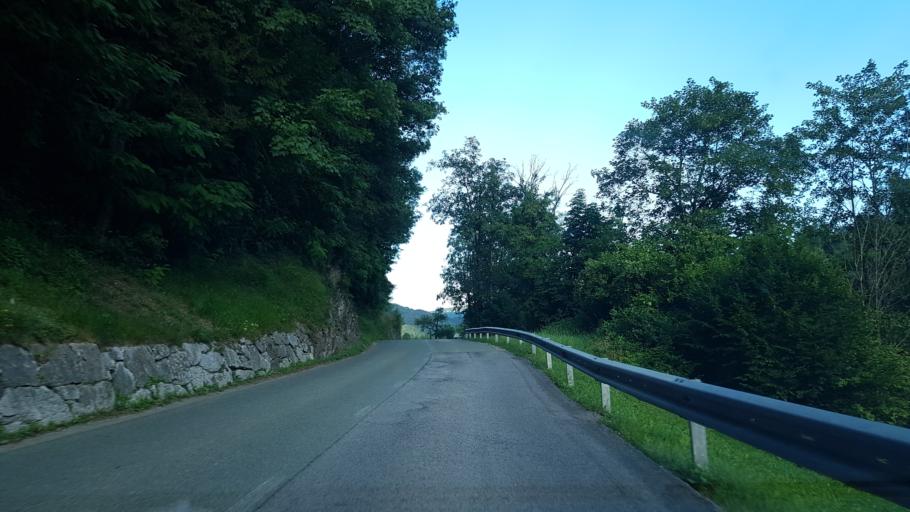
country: SI
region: Gorenja Vas-Poljane
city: Gorenja Vas
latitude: 46.1073
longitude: 14.1267
